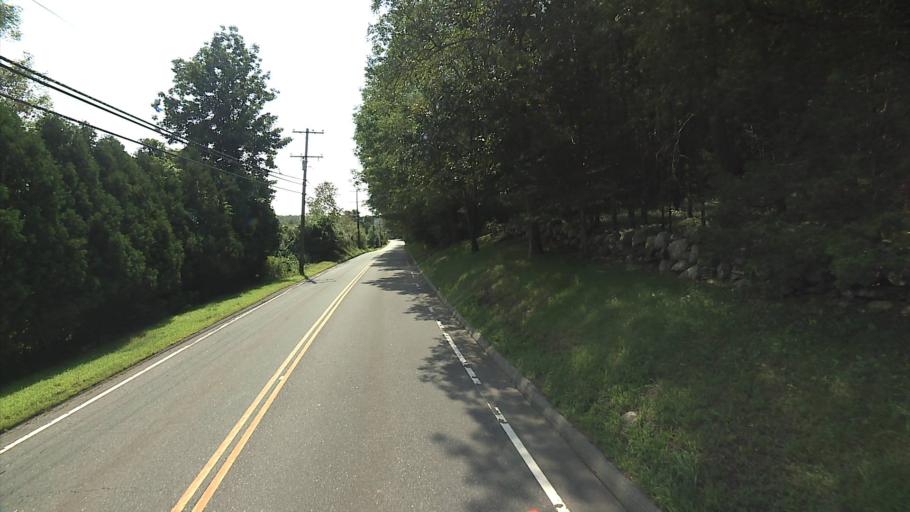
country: US
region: Connecticut
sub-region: New London County
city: Montville Center
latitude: 41.5729
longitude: -72.1810
